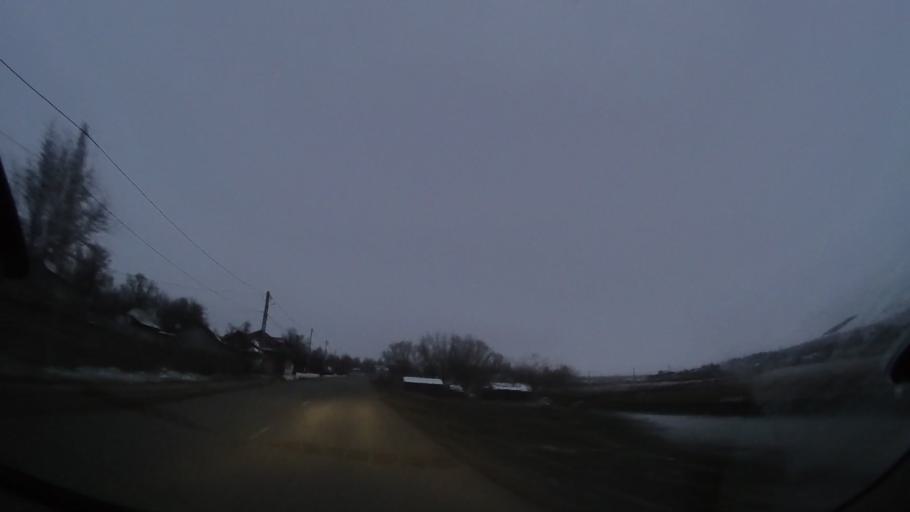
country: RO
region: Vaslui
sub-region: Comuna Vutcani
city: Vutcani
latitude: 46.4540
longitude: 28.0217
